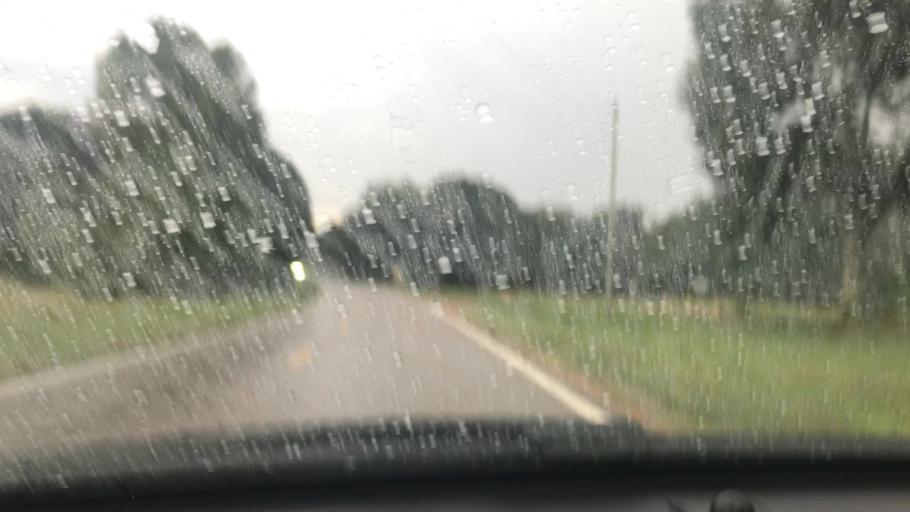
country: US
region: Mississippi
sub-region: Pike County
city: Summit
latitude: 31.3224
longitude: -90.5419
